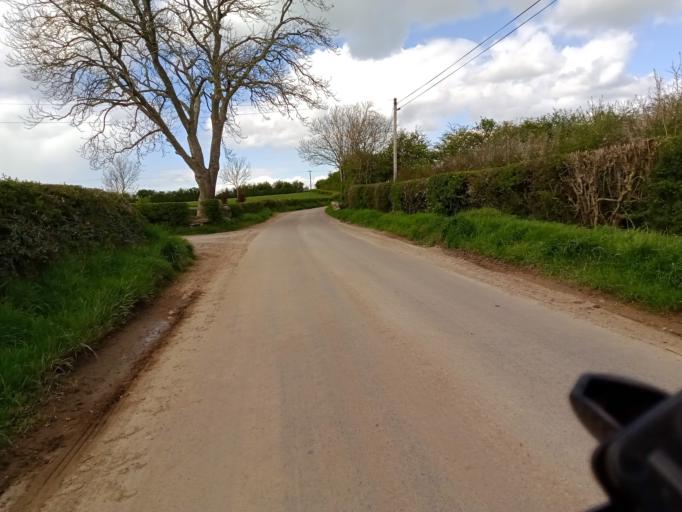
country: IE
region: Leinster
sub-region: Kilkenny
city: Thomastown
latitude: 52.5938
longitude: -7.1502
